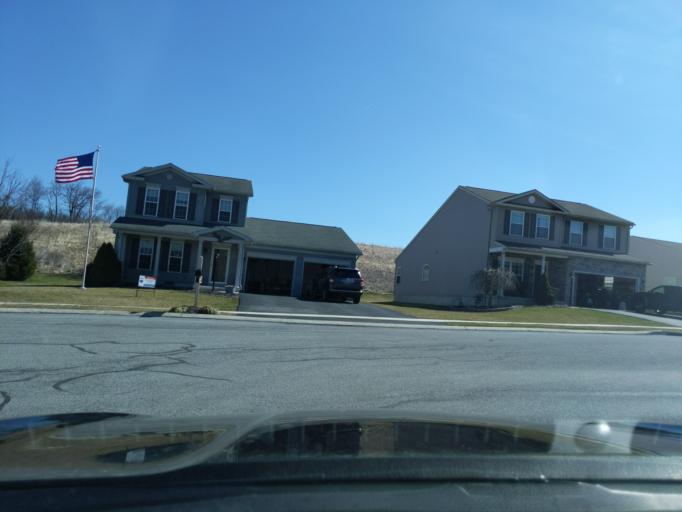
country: US
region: Pennsylvania
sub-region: Blair County
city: Duncansville
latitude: 40.4245
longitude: -78.4210
